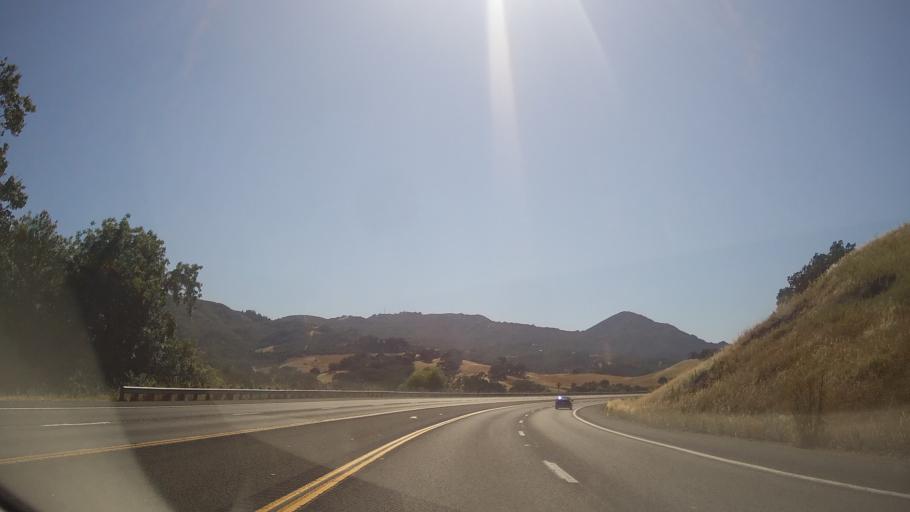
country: US
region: California
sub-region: Sonoma County
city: Cloverdale
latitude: 38.9404
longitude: -123.0742
